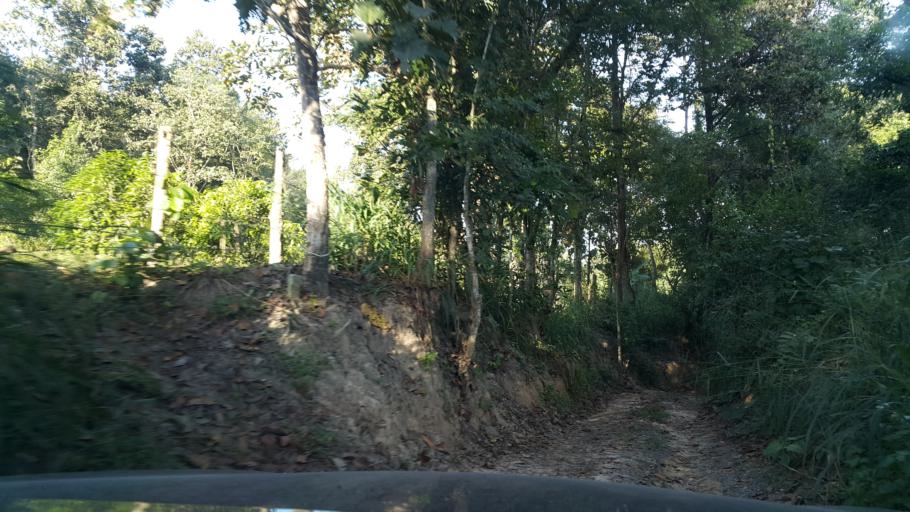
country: TH
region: Chiang Mai
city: Mae On
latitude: 18.7112
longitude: 99.1986
